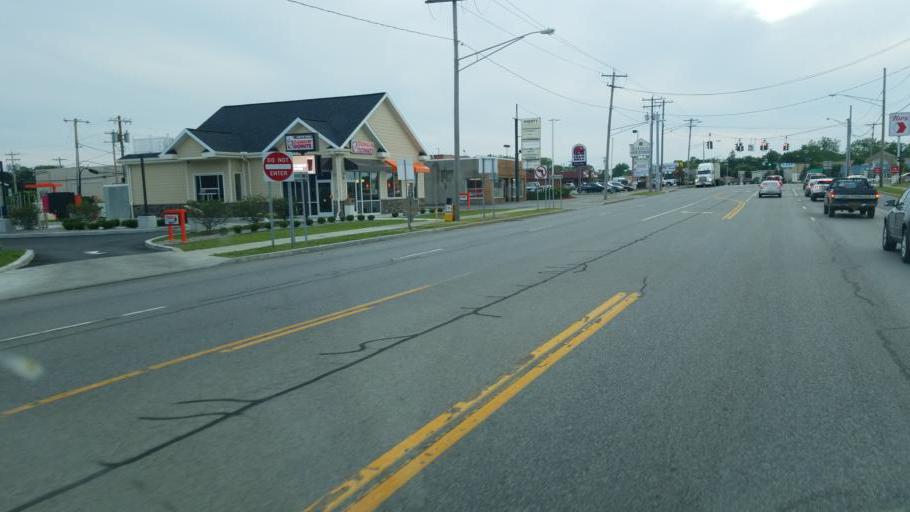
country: US
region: New York
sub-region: Genesee County
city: Batavia
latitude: 43.0050
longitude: -78.2031
